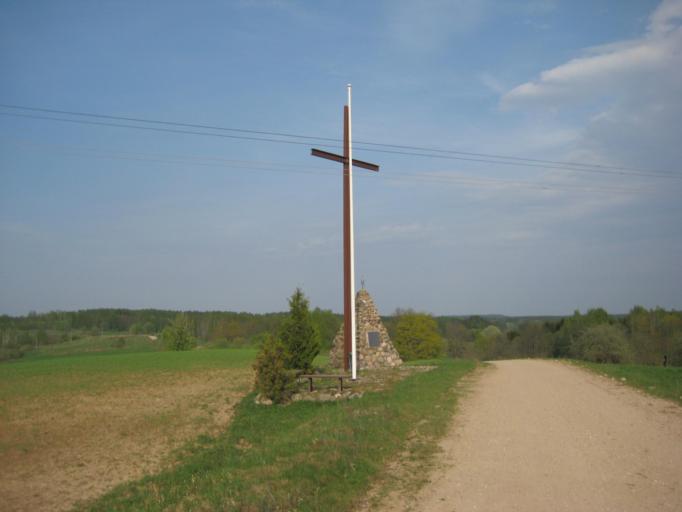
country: LT
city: Ignalina
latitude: 55.5825
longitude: 25.9886
